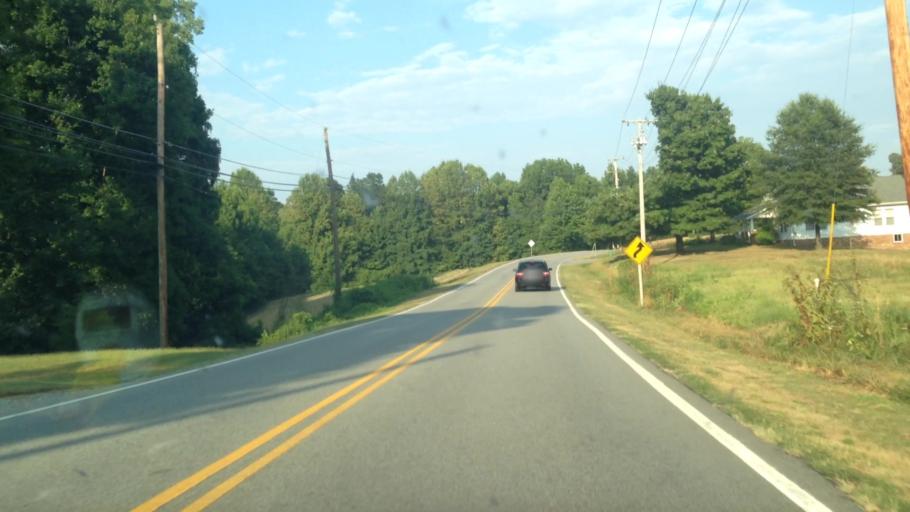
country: US
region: North Carolina
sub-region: Davidson County
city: Thomasville
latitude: 35.9403
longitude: -80.0710
